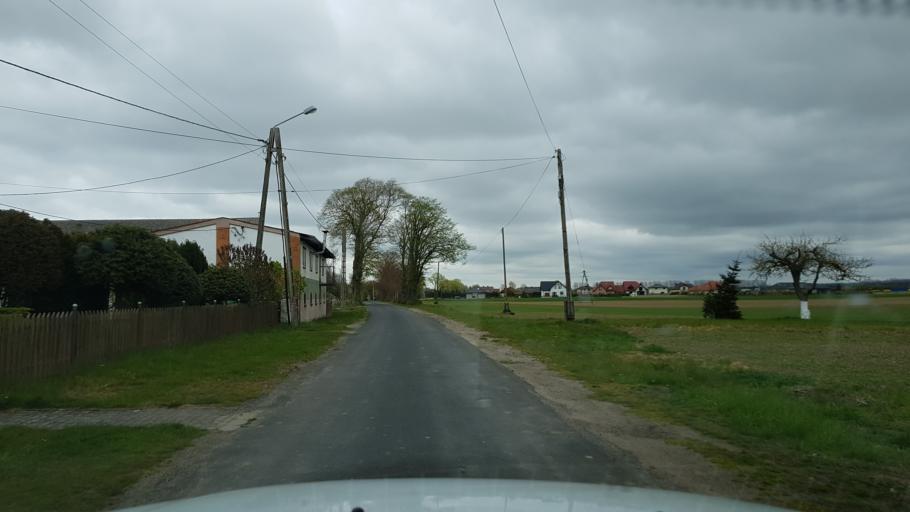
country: PL
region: West Pomeranian Voivodeship
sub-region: Powiat koszalinski
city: Mielno
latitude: 54.2324
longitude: 16.0471
